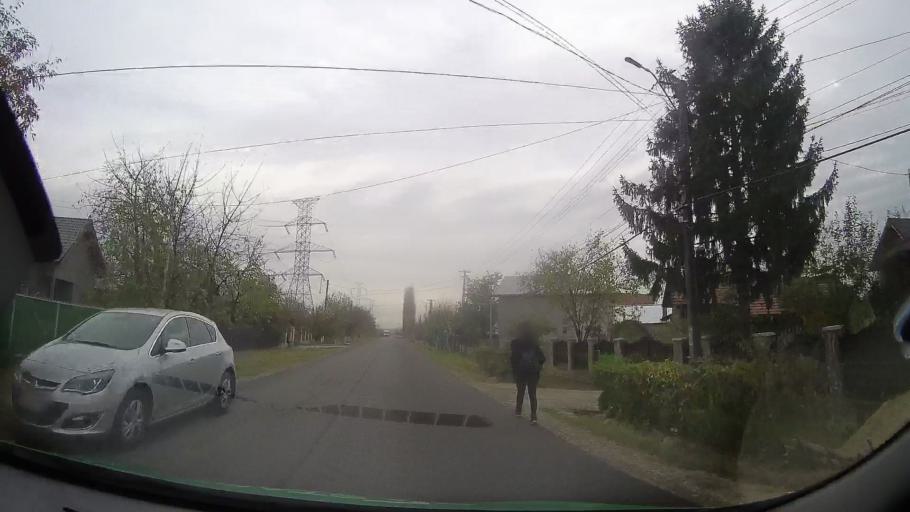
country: RO
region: Prahova
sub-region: Comuna Valea Calugareasca
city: Pantazi
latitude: 44.9302
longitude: 26.1453
